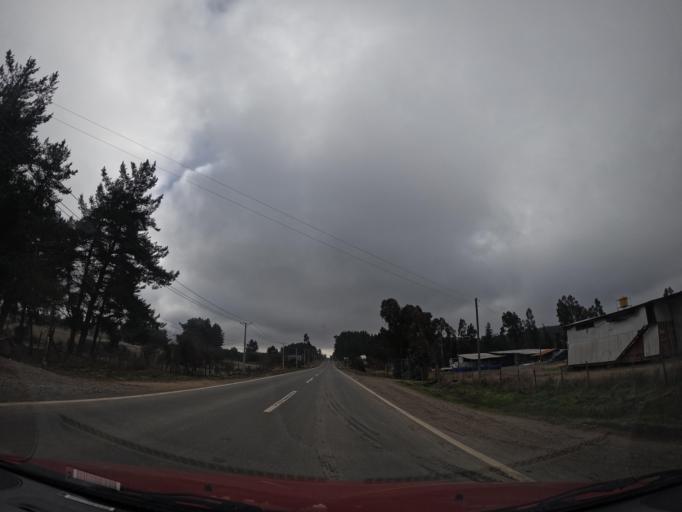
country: CL
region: Maule
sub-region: Provincia de Cauquenes
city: Cauquenes
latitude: -36.2605
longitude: -72.5481
